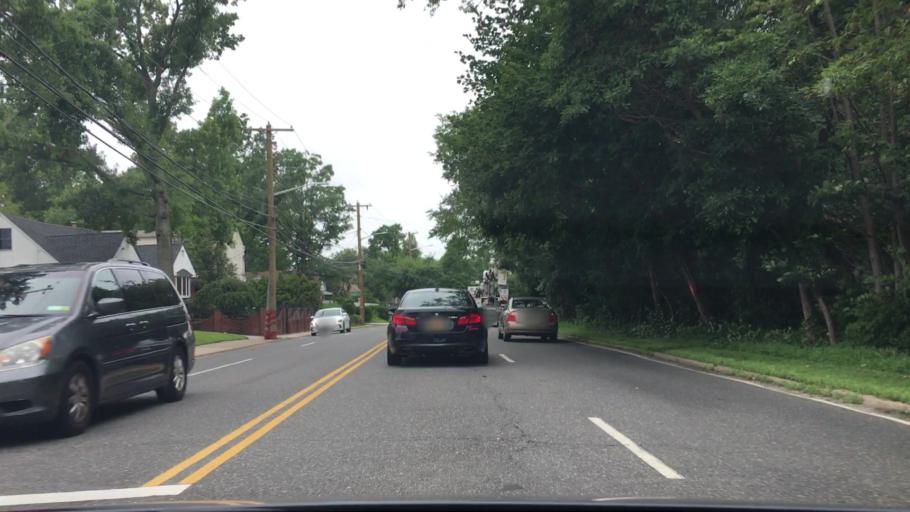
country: US
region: New York
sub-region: Nassau County
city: North Valley Stream
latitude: 40.6804
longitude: -73.6898
